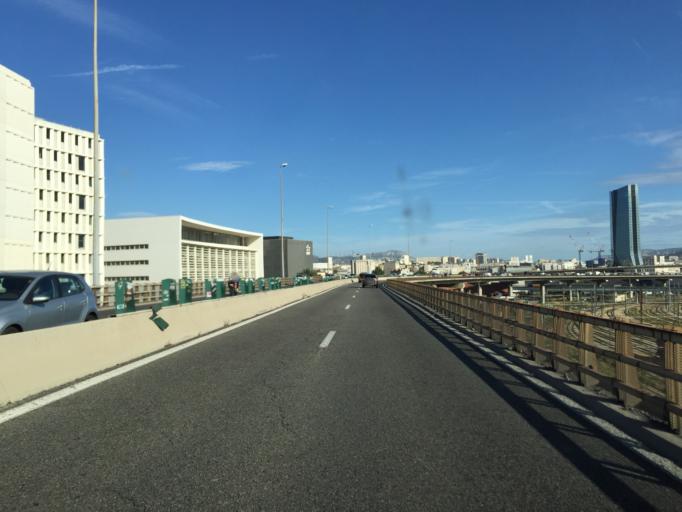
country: FR
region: Provence-Alpes-Cote d'Azur
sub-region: Departement des Bouches-du-Rhone
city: Marseille 03
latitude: 43.3239
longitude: 5.3628
